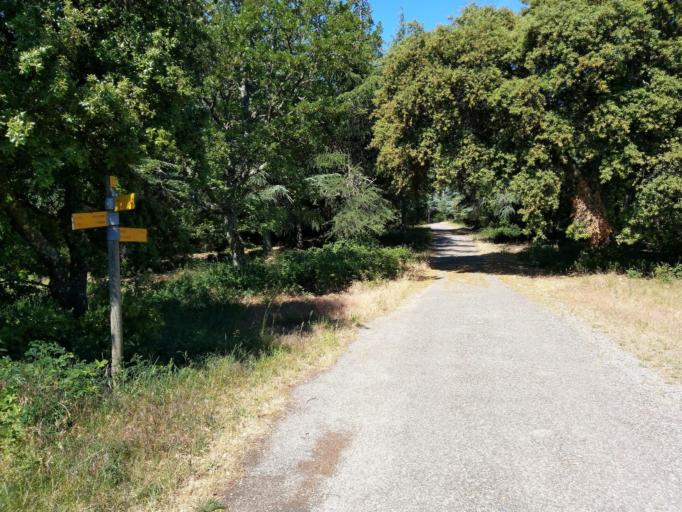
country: FR
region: Provence-Alpes-Cote d'Azur
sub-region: Departement du Vaucluse
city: Menerbes
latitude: 43.7971
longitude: 5.2208
